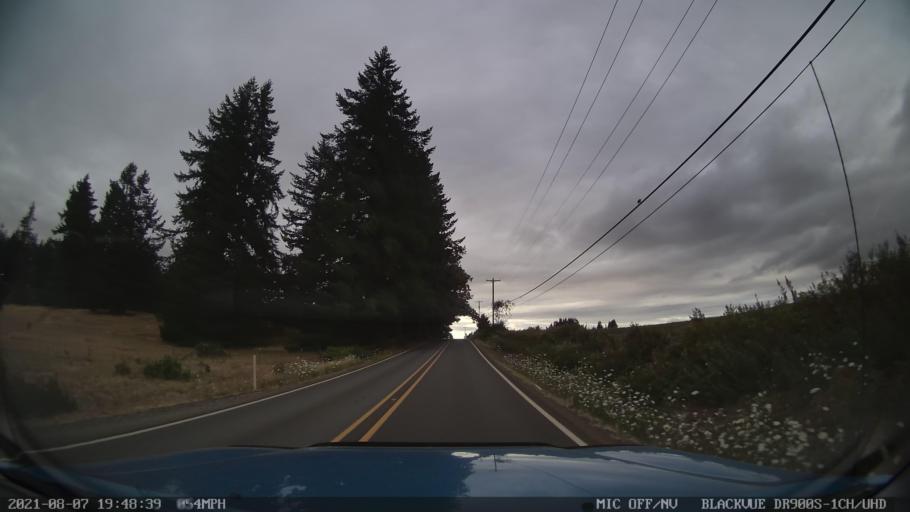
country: US
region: Oregon
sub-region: Marion County
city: Silverton
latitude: 44.9770
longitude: -122.7160
